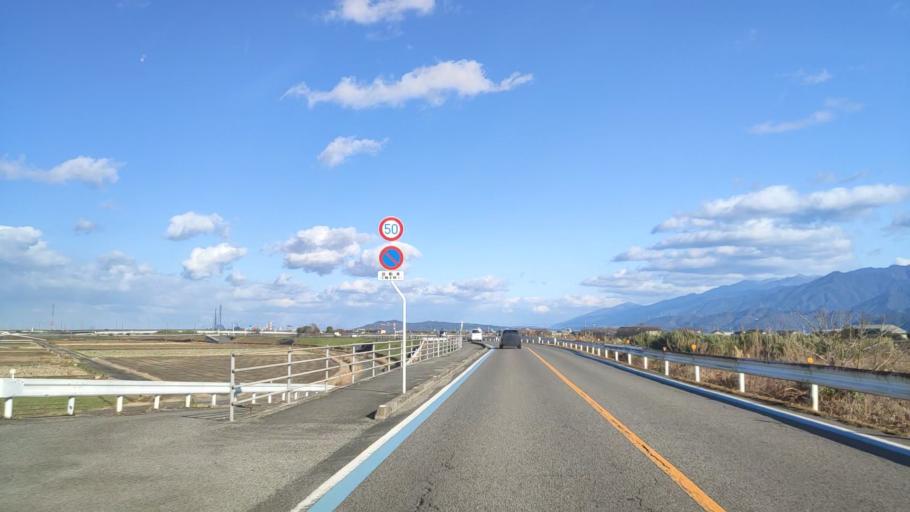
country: JP
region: Ehime
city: Saijo
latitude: 33.9068
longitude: 133.1238
